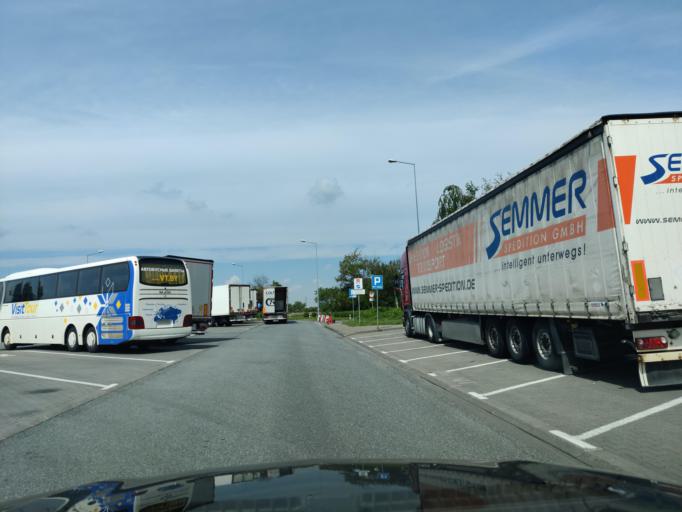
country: PL
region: Greater Poland Voivodeship
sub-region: Powiat poznanski
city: Kleszczewo
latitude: 52.3296
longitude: 17.0907
